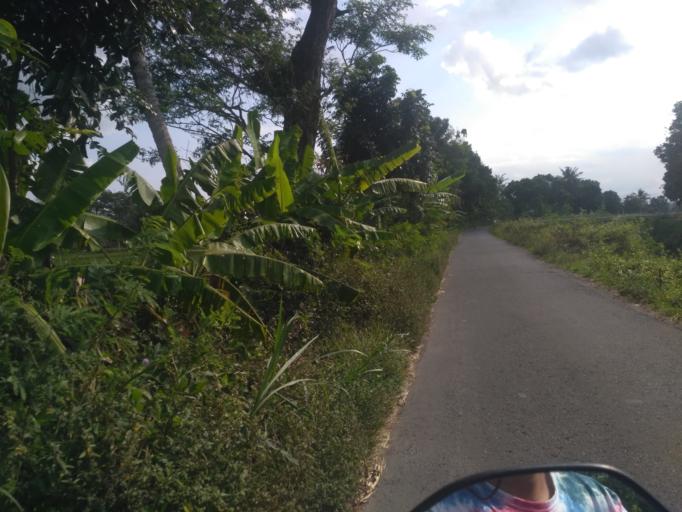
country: ID
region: Daerah Istimewa Yogyakarta
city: Godean
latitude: -7.7423
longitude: 110.3147
